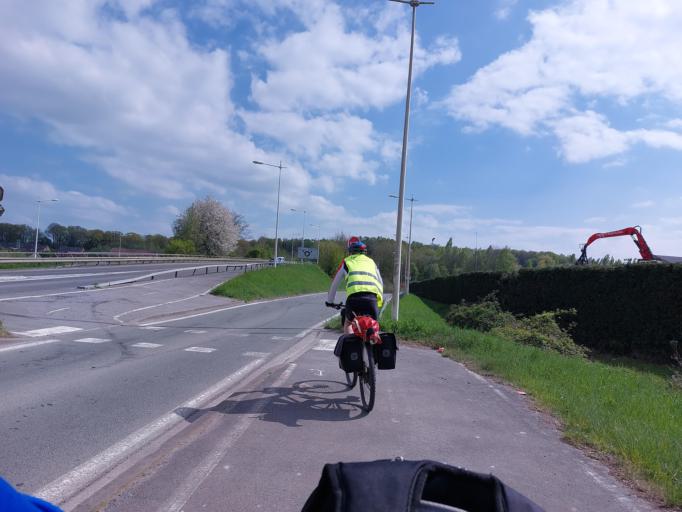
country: FR
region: Nord-Pas-de-Calais
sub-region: Departement du Nord
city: Hautmont
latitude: 50.2478
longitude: 3.9019
